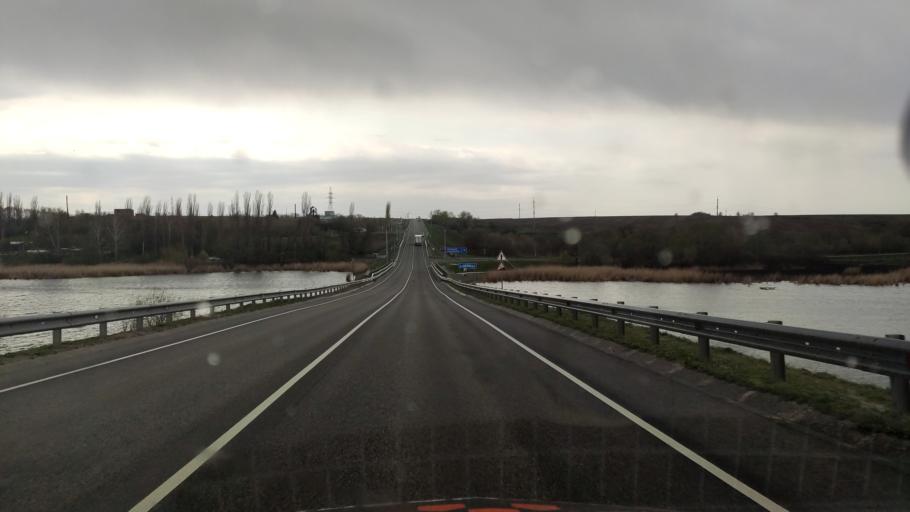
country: RU
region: Voronezj
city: Nizhnedevitsk
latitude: 51.5646
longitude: 38.3695
